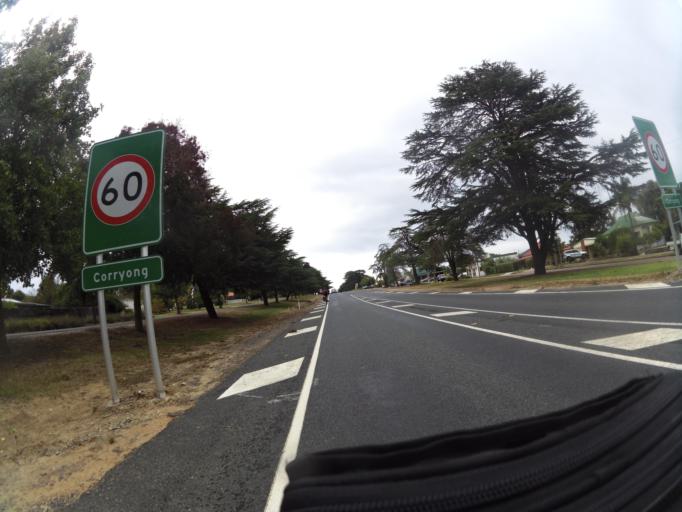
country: AU
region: New South Wales
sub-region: Snowy River
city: Jindabyne
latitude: -36.1904
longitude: 147.9129
